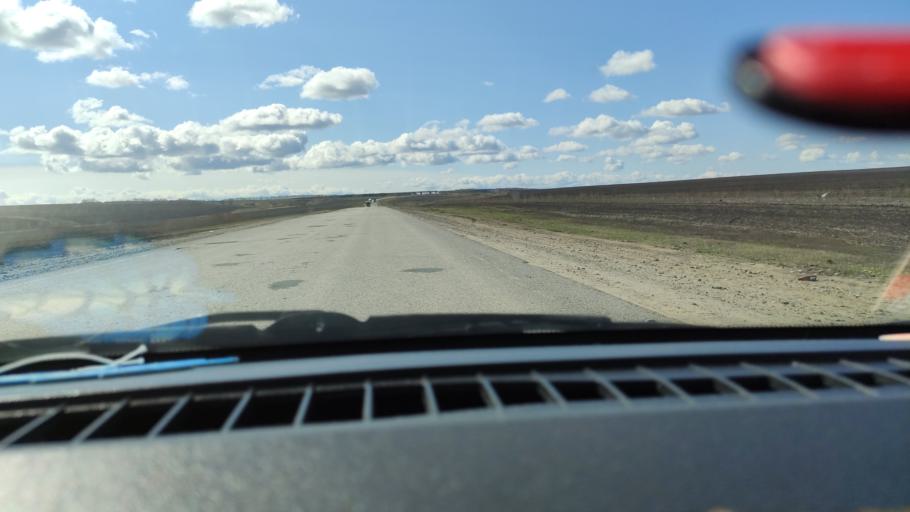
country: RU
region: Samara
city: Varlamovo
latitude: 53.0113
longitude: 48.3324
